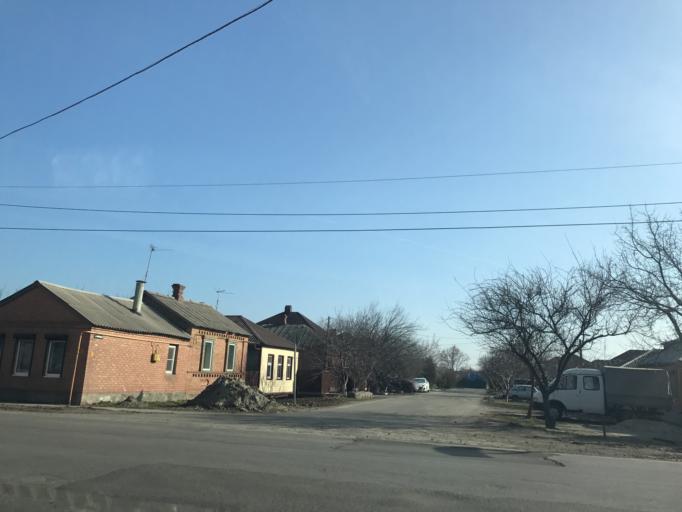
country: RU
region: Rostov
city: Bataysk
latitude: 47.1351
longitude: 39.7471
